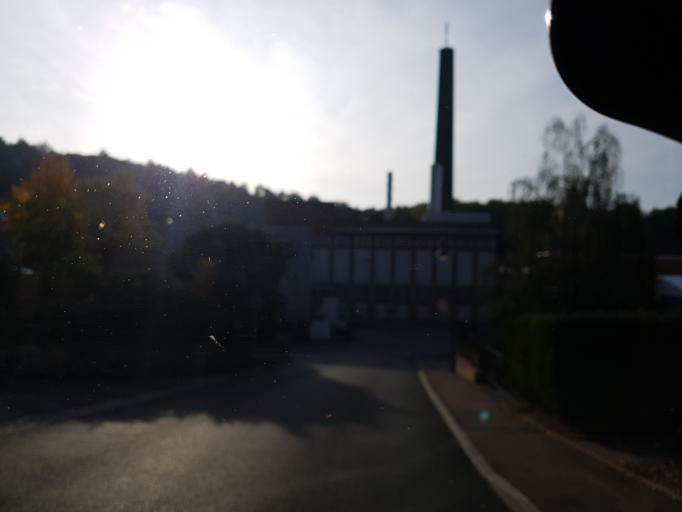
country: DE
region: Saxony
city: Kriebstein
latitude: 51.0479
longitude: 13.0182
